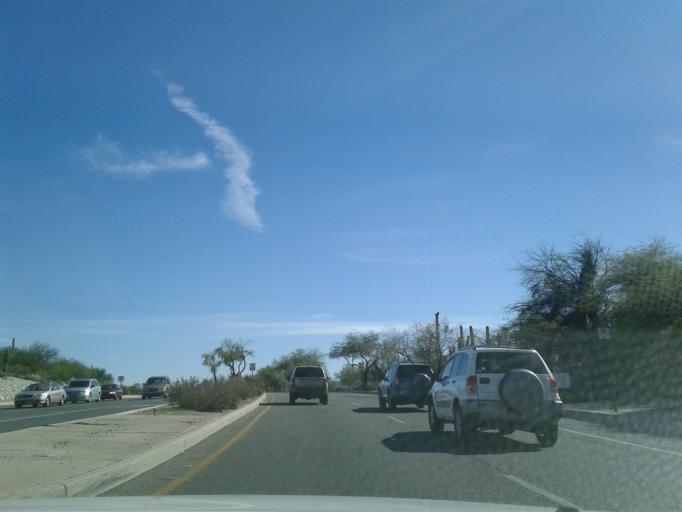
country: US
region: Arizona
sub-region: Pima County
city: Catalina Foothills
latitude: 32.3126
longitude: -110.9120
